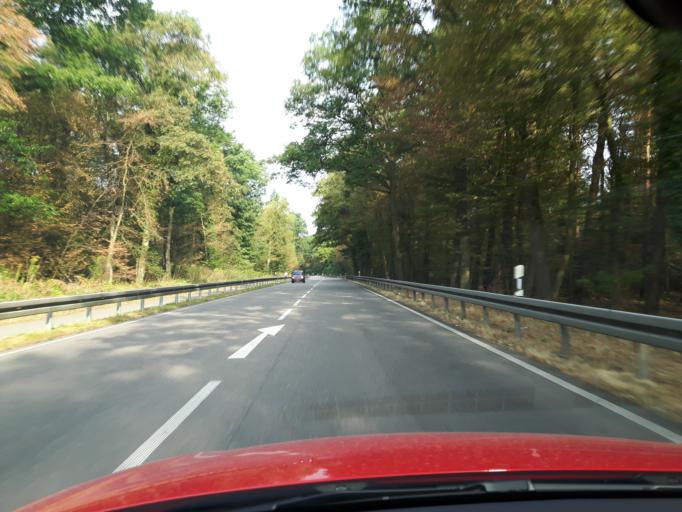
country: DE
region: Baden-Wuerttemberg
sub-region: Karlsruhe Region
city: Ettlingen
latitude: 48.9536
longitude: 8.3615
